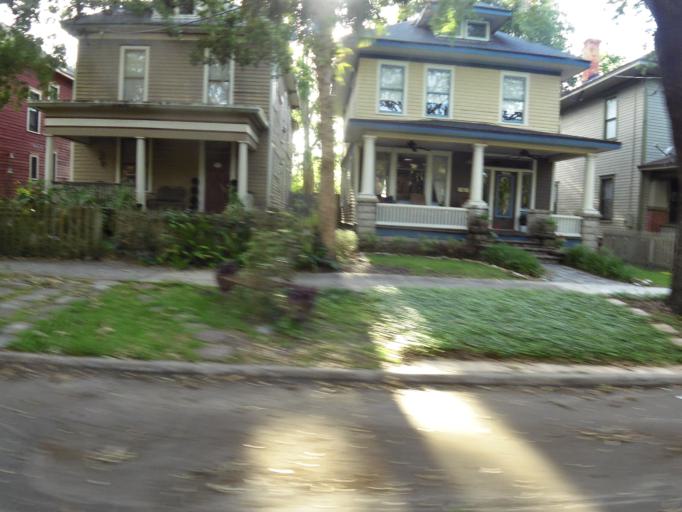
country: US
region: Florida
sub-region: Duval County
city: Jacksonville
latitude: 30.3469
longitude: -81.6570
